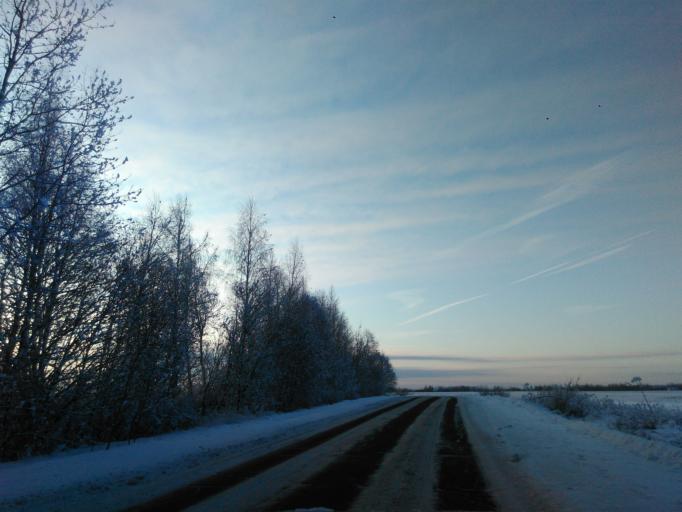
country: RU
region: Tverskaya
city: Zavidovo
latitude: 56.6223
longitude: 36.6150
